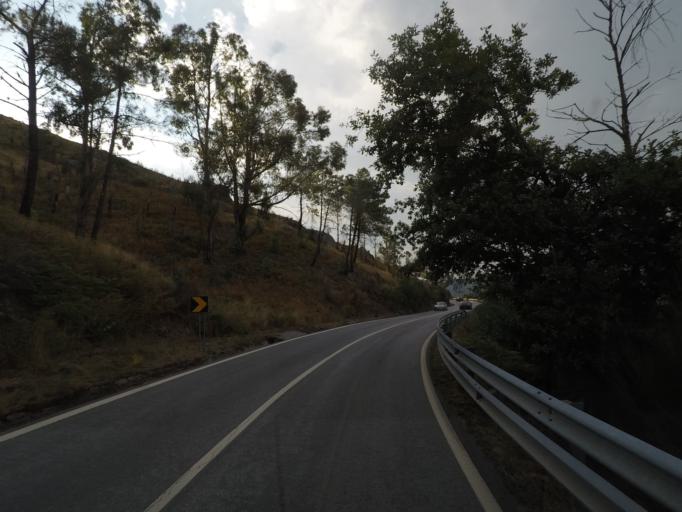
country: PT
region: Porto
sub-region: Baiao
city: Valadares
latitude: 41.1997
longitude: -7.9556
